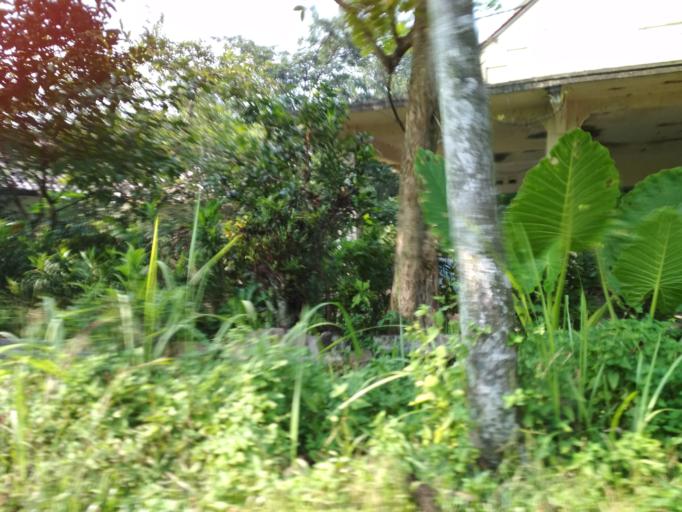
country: ID
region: West Java
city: Ciampea
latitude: -6.5562
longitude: 106.7268
